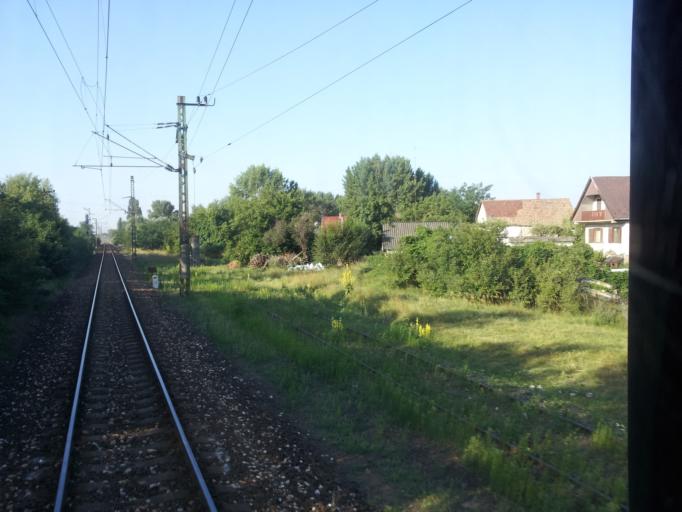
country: HU
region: Pest
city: Taksony
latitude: 47.3148
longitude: 19.0755
